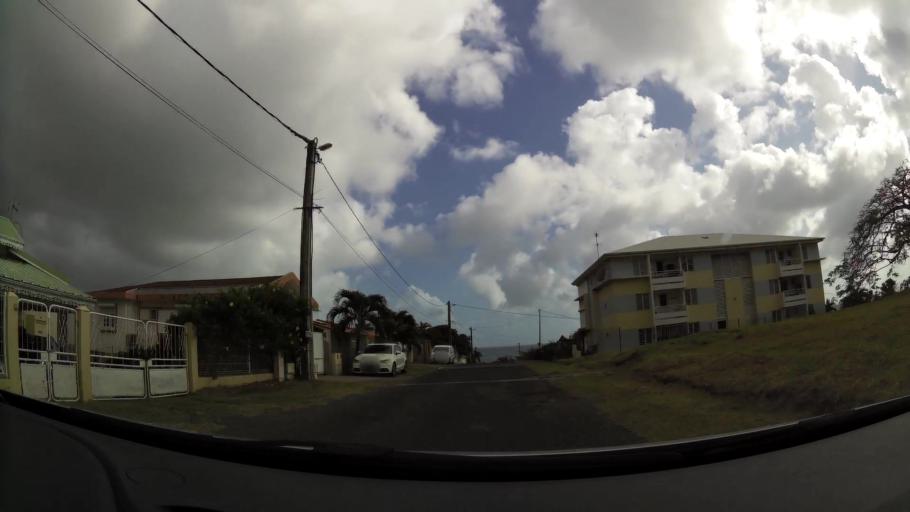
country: MQ
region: Martinique
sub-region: Martinique
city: Sainte-Luce
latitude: 14.4678
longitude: -60.9259
